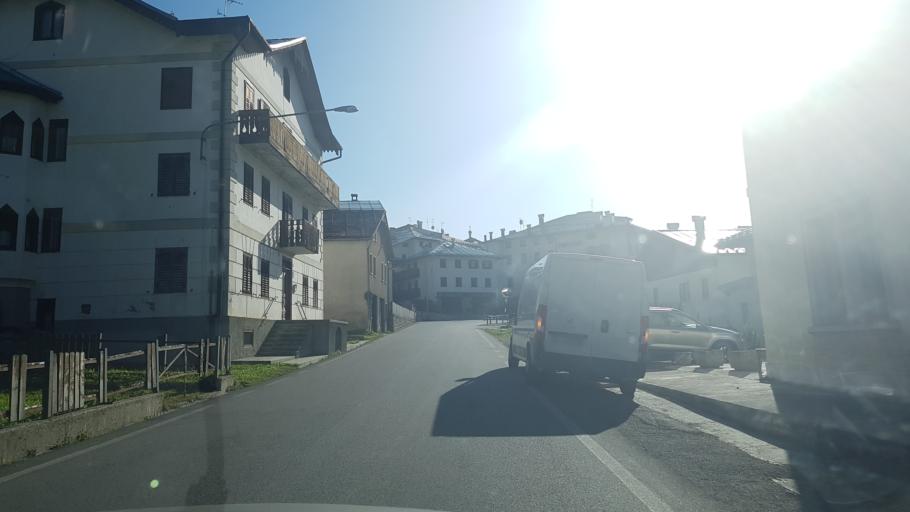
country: IT
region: Veneto
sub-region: Provincia di Belluno
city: Candide
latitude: 46.6010
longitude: 12.4899
